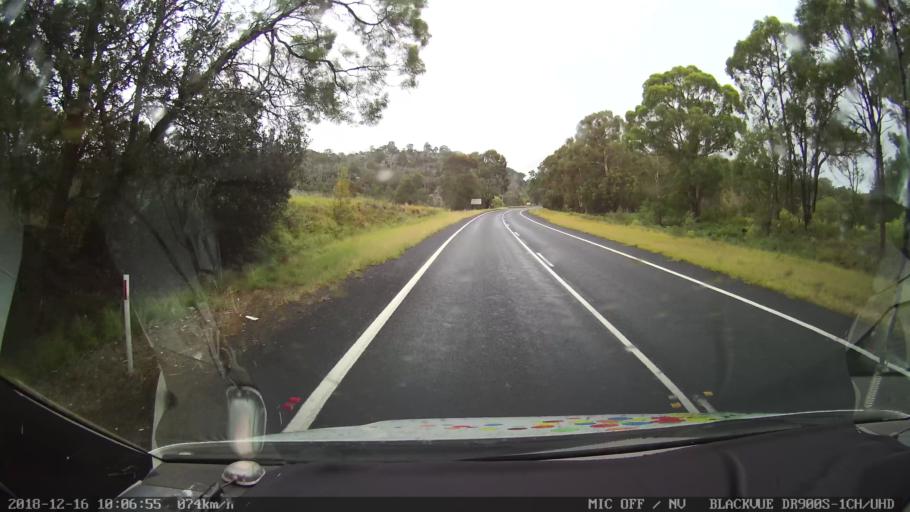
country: AU
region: New South Wales
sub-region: Glen Innes Severn
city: Glen Innes
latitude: -29.3401
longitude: 151.8927
